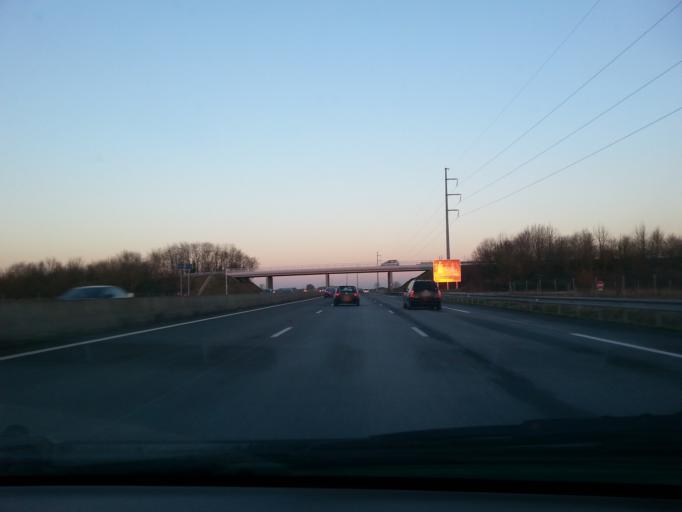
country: FR
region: Centre
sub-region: Departement d'Eure-et-Loir
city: Bailleau-le-Pin
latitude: 48.3321
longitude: 1.3893
